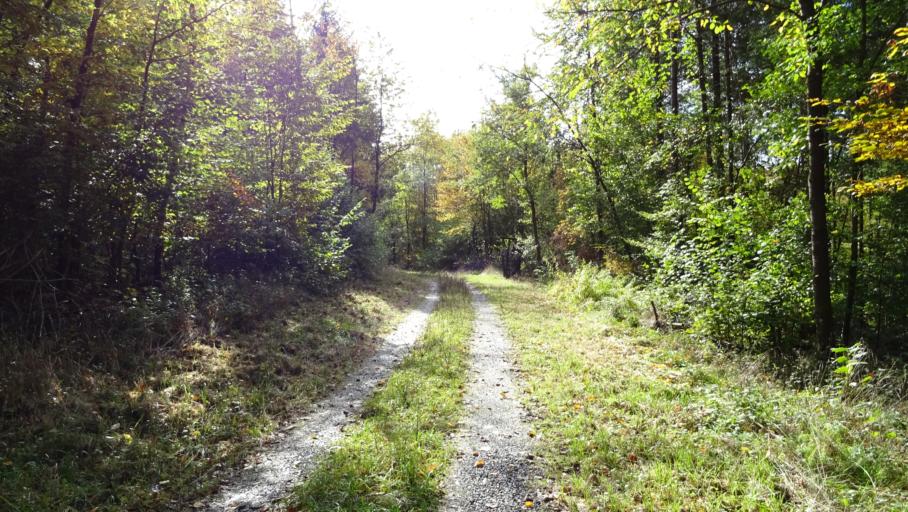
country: DE
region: Baden-Wuerttemberg
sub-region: Karlsruhe Region
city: Billigheim
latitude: 49.3684
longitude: 9.2665
